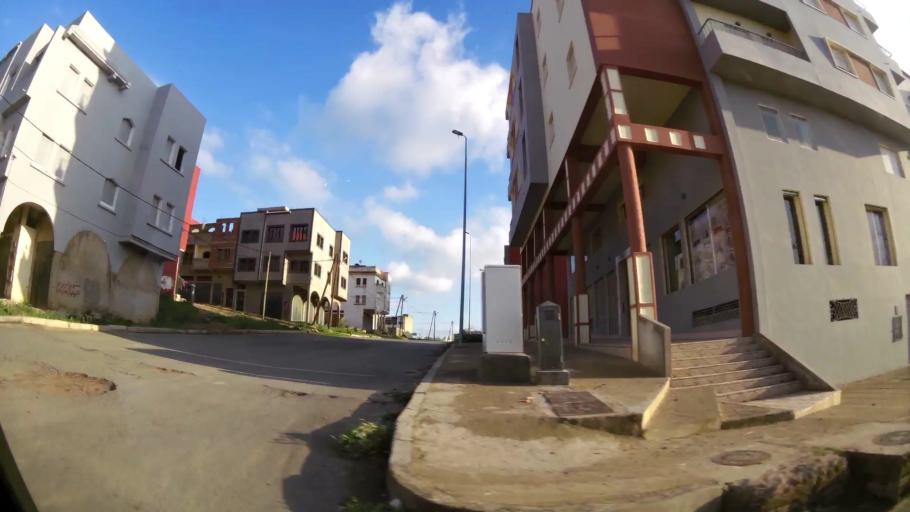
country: MA
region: Chaouia-Ouardigha
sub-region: Settat Province
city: Settat
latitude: 33.0016
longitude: -7.6004
